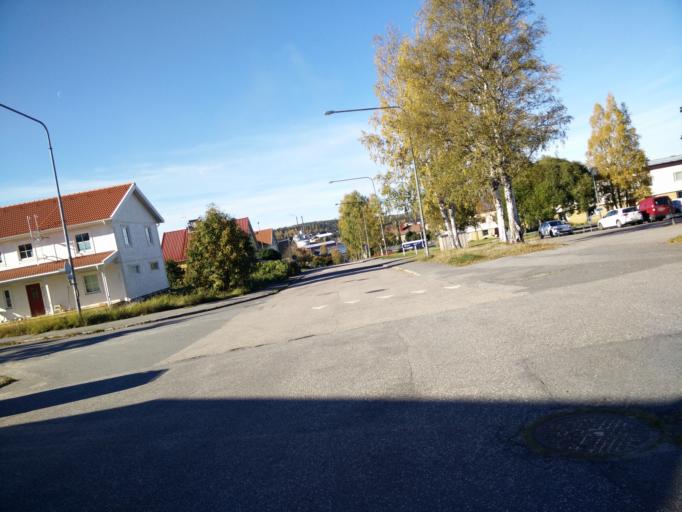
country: SE
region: Vaesternorrland
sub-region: Haernoesands Kommun
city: Haernoesand
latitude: 62.6403
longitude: 17.9607
